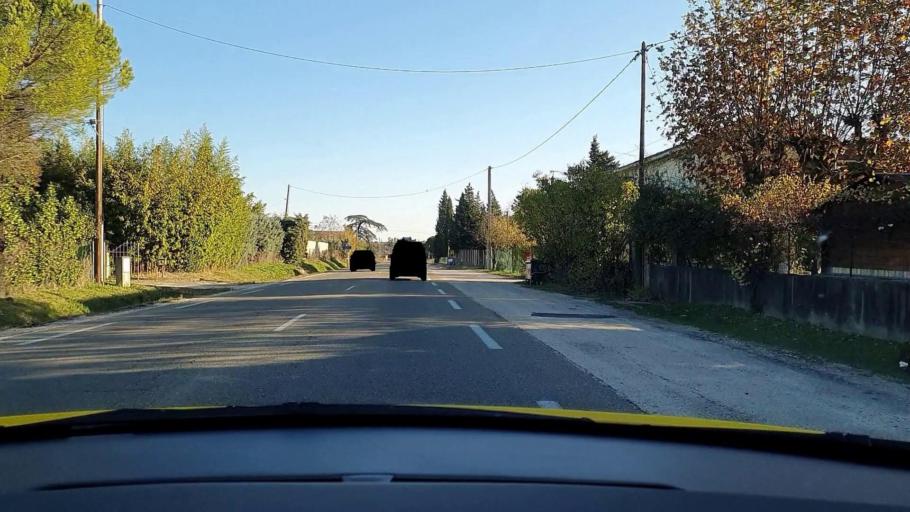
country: FR
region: Languedoc-Roussillon
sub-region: Departement du Gard
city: Saint-Julien-les-Rosiers
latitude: 44.1638
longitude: 4.1248
